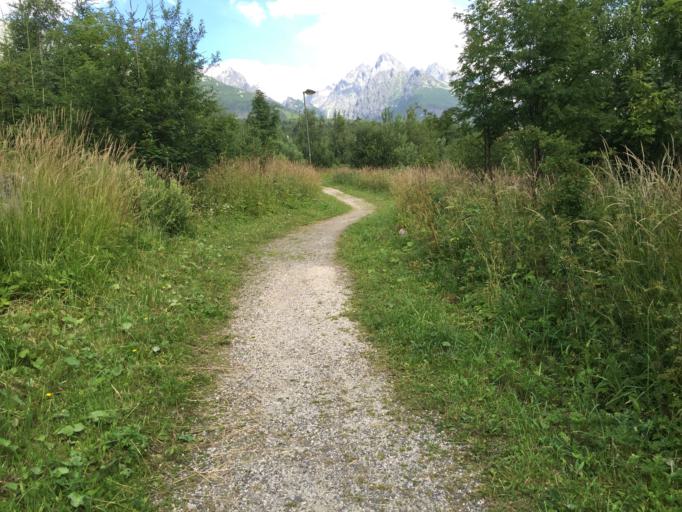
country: SK
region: Presovsky
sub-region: Okres Poprad
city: Vysoke Tatry
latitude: 49.1354
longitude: 20.2382
